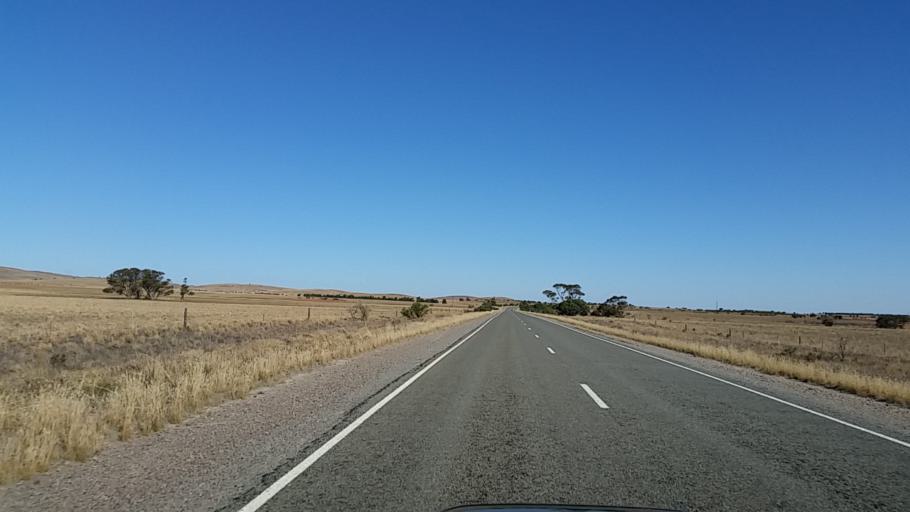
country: AU
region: South Australia
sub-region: Peterborough
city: Peterborough
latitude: -32.5375
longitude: 138.5573
